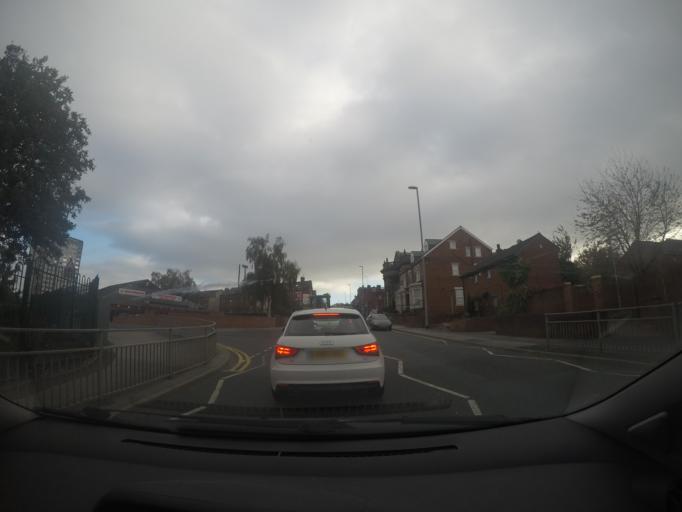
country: GB
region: England
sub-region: City and Borough of Leeds
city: Leeds
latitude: 53.7868
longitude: -1.5617
